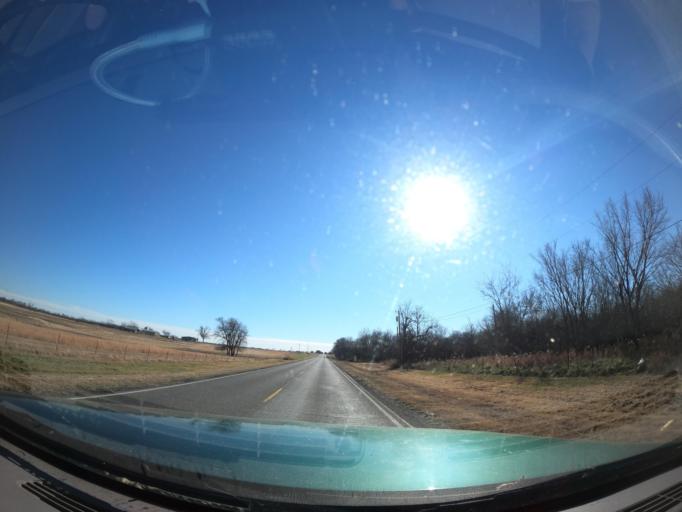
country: US
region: Oklahoma
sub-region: Muskogee County
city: Haskell
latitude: 35.6779
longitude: -95.6422
